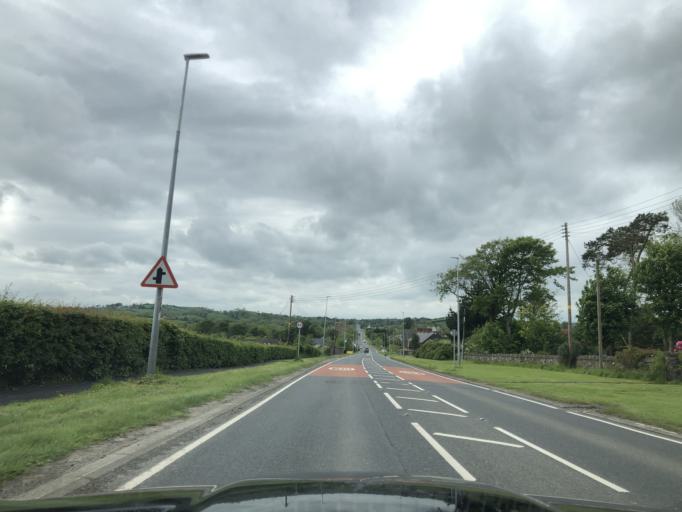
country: GB
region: Northern Ireland
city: Crossgar
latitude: 54.3616
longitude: -5.7659
